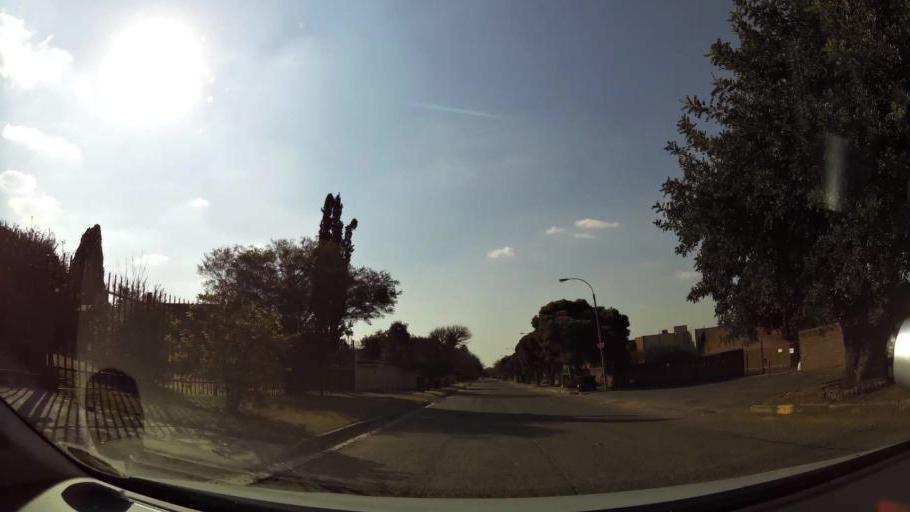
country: ZA
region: Gauteng
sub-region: City of Johannesburg Metropolitan Municipality
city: Modderfontein
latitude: -26.0942
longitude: 28.2156
